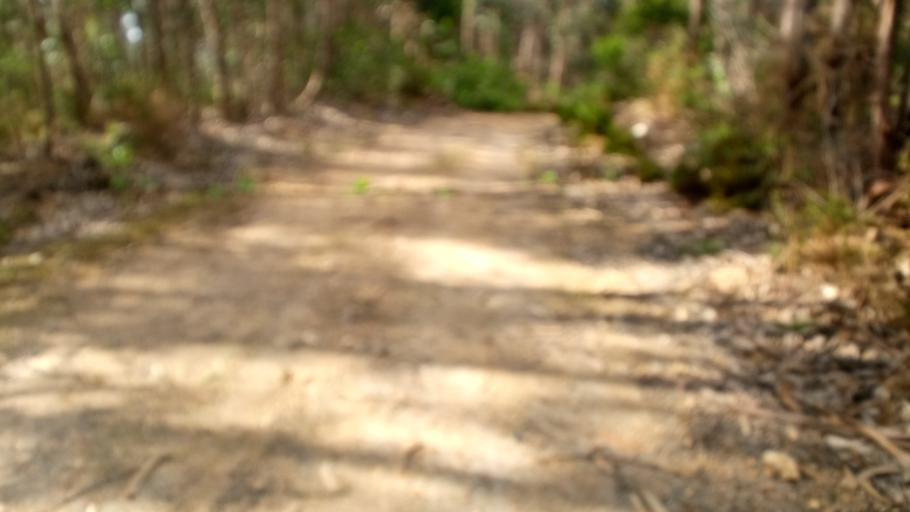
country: PT
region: Leiria
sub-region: Obidos
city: Obidos
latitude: 39.3900
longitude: -9.2085
